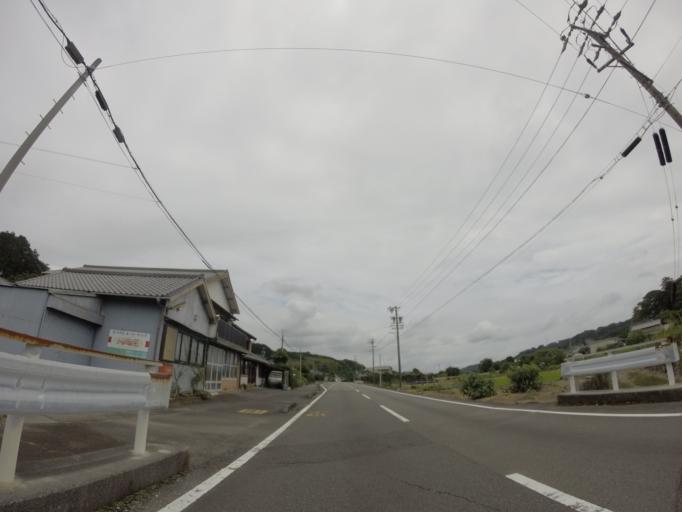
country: JP
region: Shizuoka
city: Shimada
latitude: 34.7795
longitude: 138.1690
